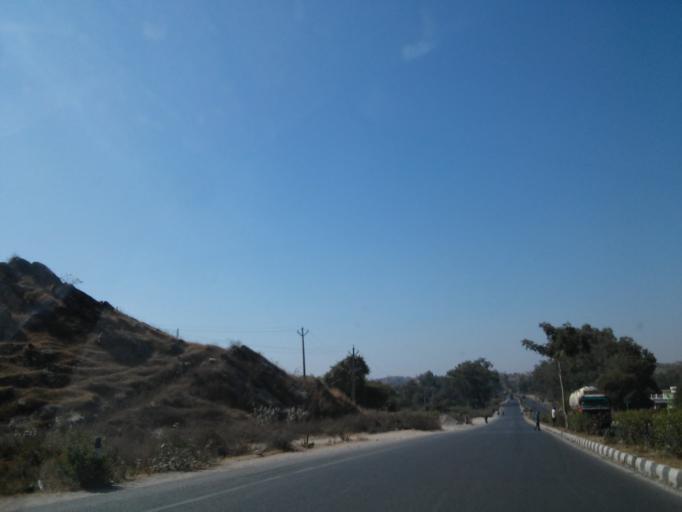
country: IN
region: Rajasthan
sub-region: Dungarpur
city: Dungarpur
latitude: 23.9174
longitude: 73.5629
